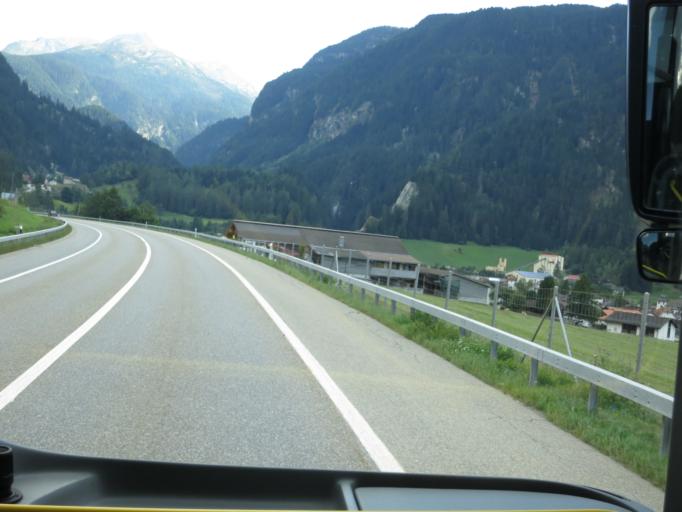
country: CH
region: Grisons
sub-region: Hinterrhein District
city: Thusis
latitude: 46.6054
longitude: 9.4308
